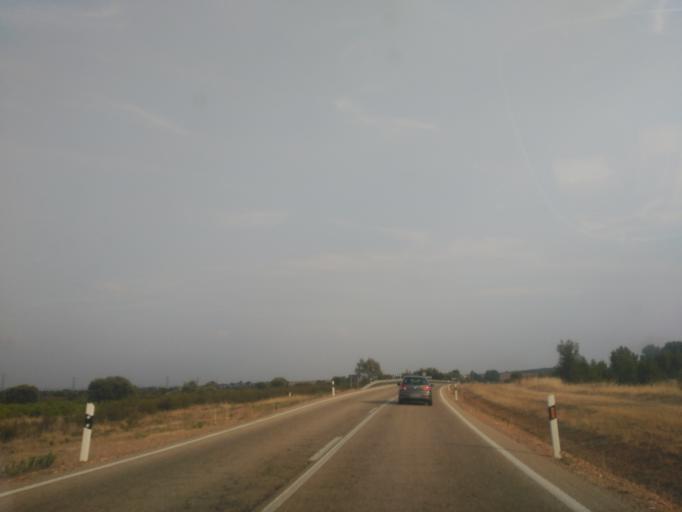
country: ES
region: Castille and Leon
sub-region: Provincia de Zamora
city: Tabara
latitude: 41.8596
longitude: -5.9953
